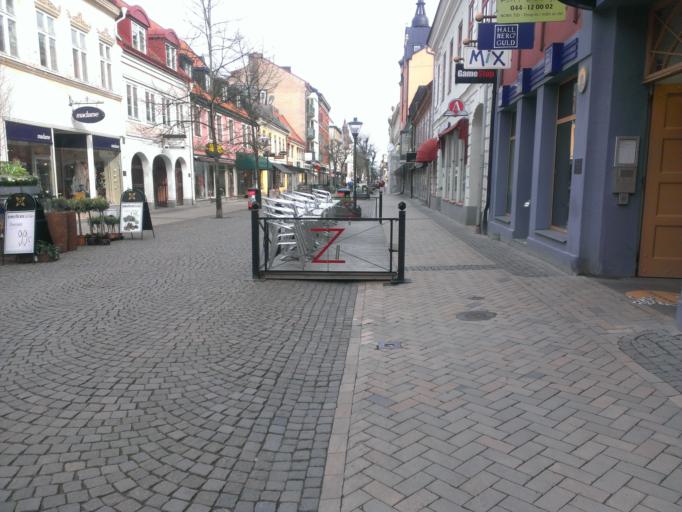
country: SE
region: Skane
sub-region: Kristianstads Kommun
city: Kristianstad
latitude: 56.0297
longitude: 14.1558
